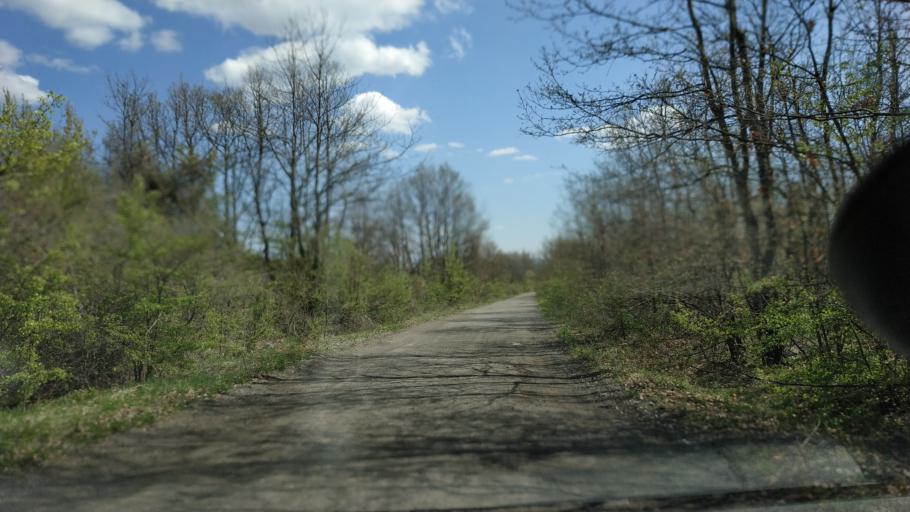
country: RS
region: Central Serbia
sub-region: Zajecarski Okrug
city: Soko Banja
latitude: 43.5429
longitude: 21.9026
